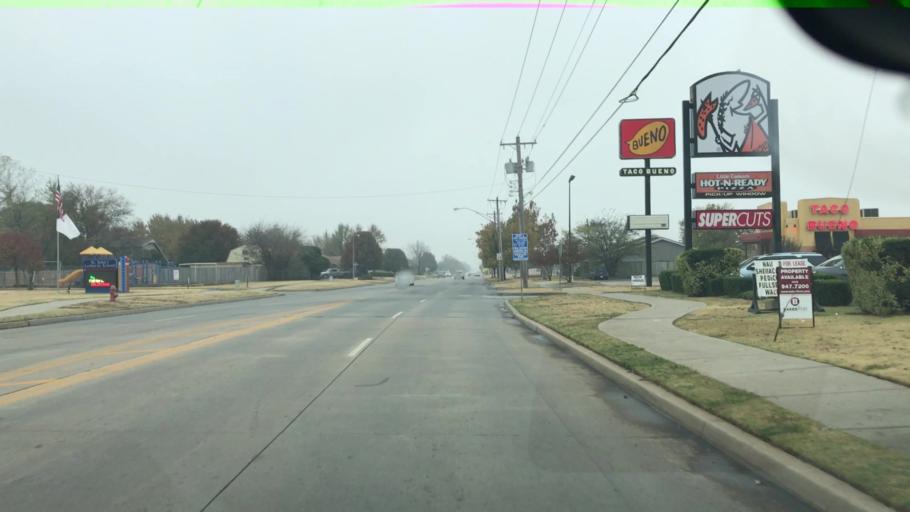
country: US
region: Oklahoma
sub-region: Cleveland County
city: Moore
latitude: 35.3482
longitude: -97.5122
